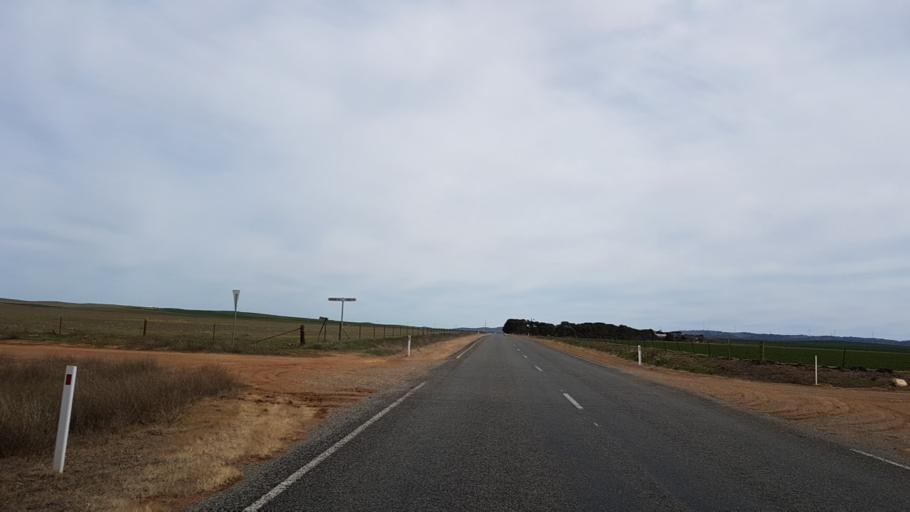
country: AU
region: South Australia
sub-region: Peterborough
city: Peterborough
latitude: -33.0171
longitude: 138.6942
